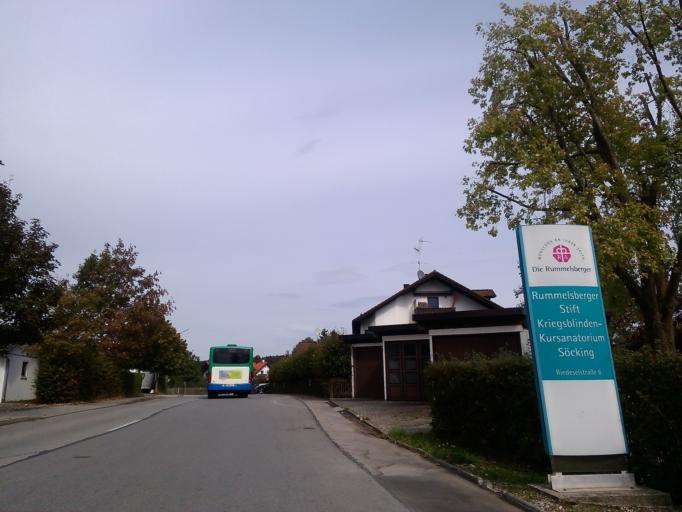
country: DE
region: Bavaria
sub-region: Upper Bavaria
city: Starnberg
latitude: 48.0047
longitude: 11.3187
